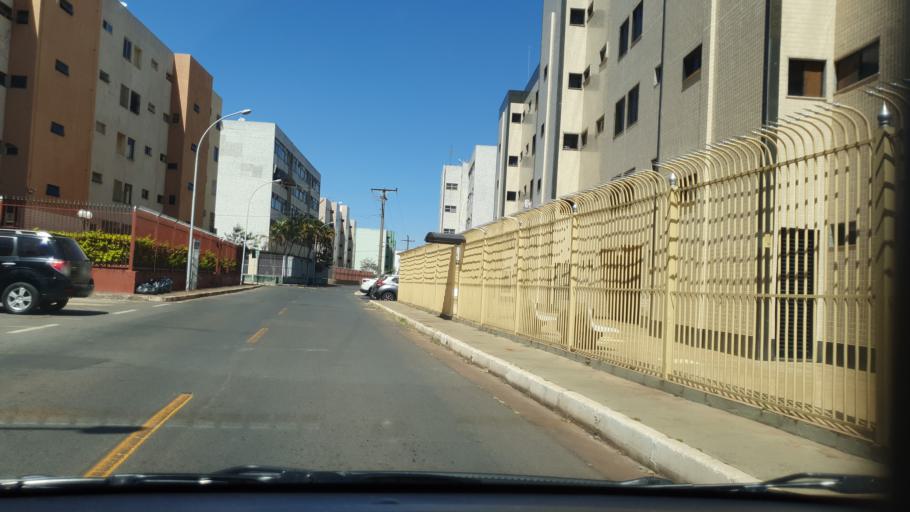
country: BR
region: Federal District
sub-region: Brasilia
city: Brasilia
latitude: -15.7939
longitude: -47.9397
